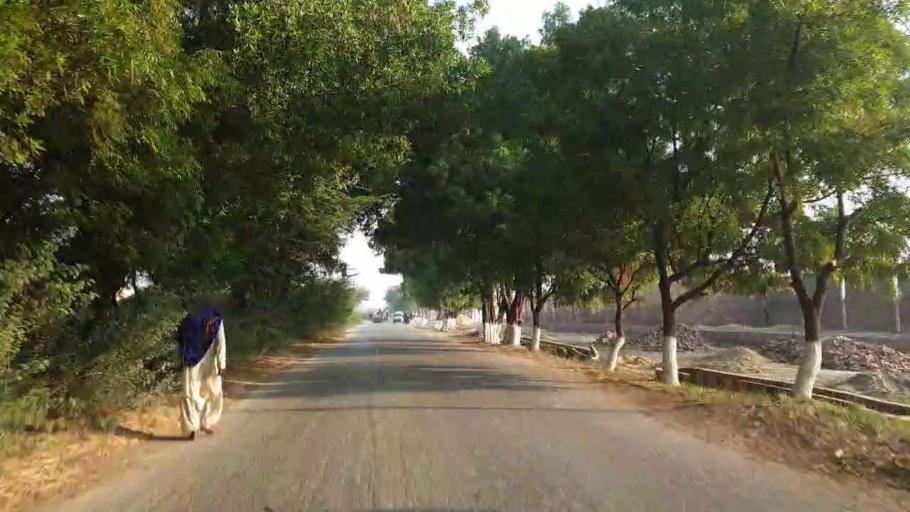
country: PK
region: Sindh
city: Tando Bago
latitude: 24.7739
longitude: 68.9599
